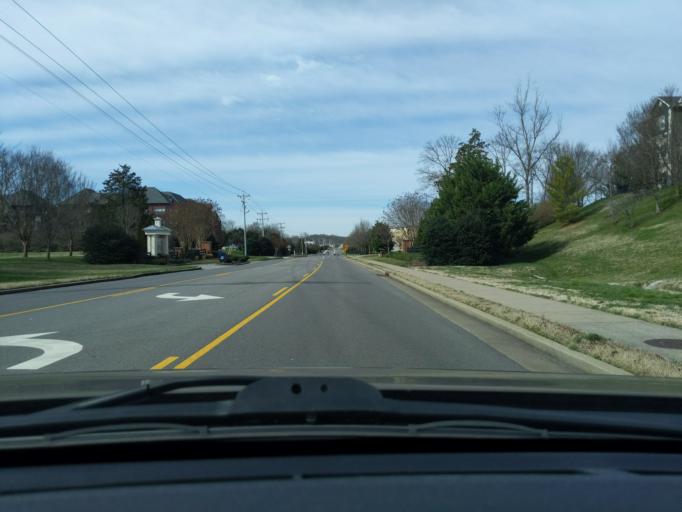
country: US
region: Tennessee
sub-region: Wilson County
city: Mount Juliet
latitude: 36.1632
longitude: -86.5062
